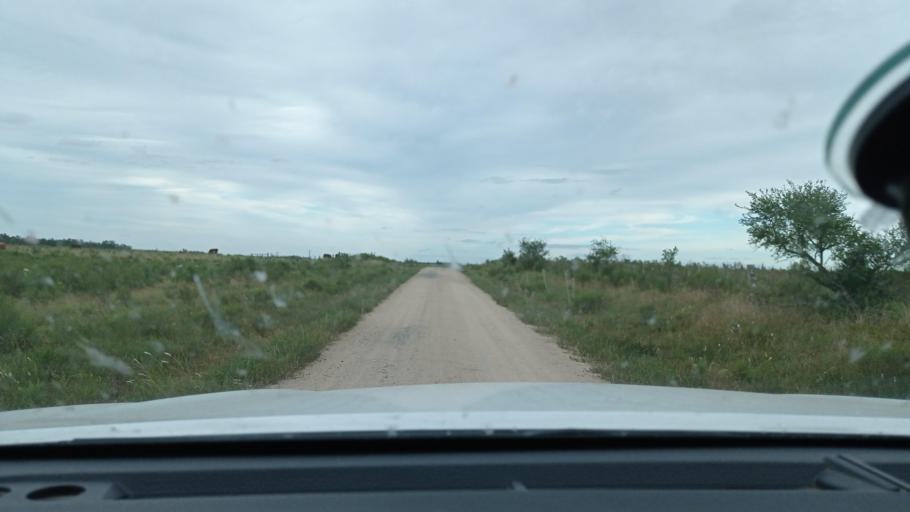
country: UY
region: Florida
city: Casupa
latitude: -34.1449
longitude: -55.7901
